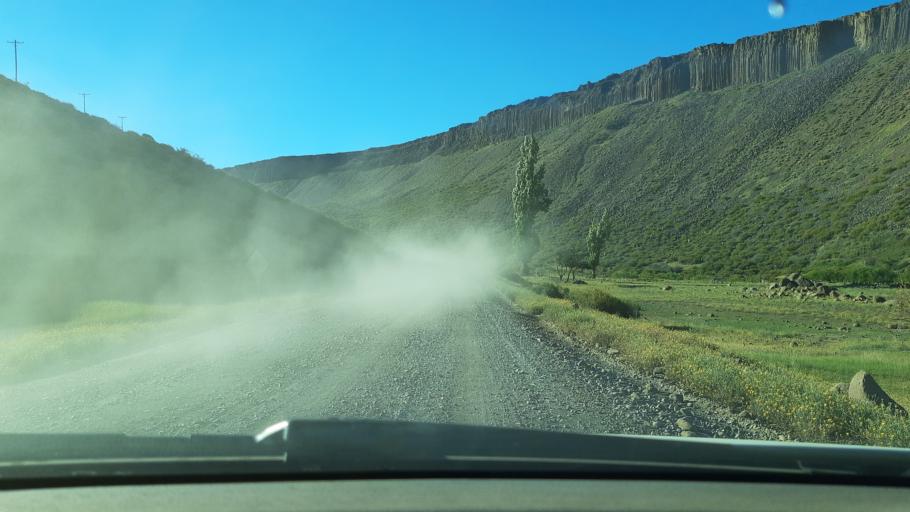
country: AR
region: Neuquen
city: Las Ovejas
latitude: -36.8158
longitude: -70.6983
